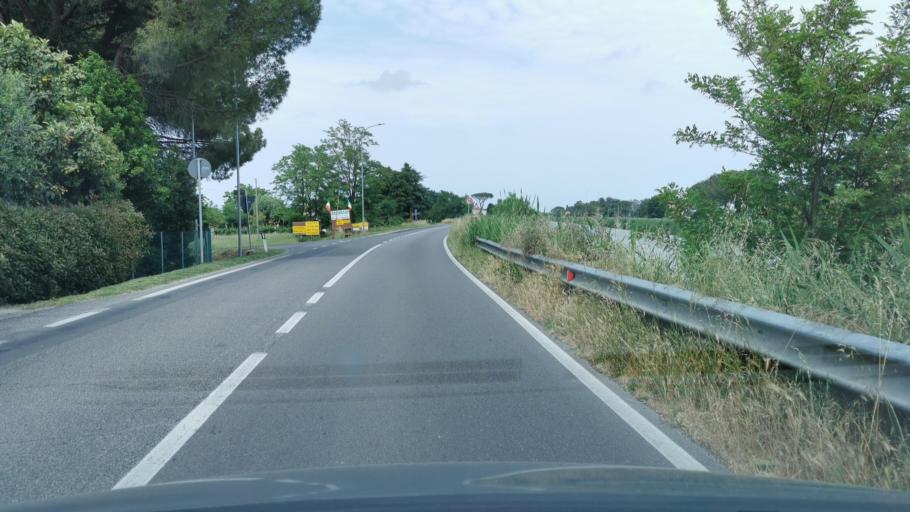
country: IT
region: Emilia-Romagna
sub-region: Provincia di Ravenna
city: Sant'Alberto
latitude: 44.5464
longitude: 12.2118
